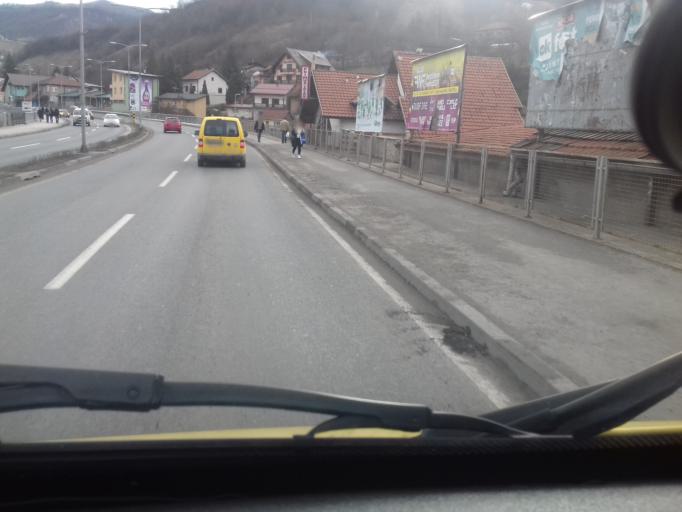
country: BA
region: Federation of Bosnia and Herzegovina
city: Zenica
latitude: 44.1988
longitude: 17.9061
